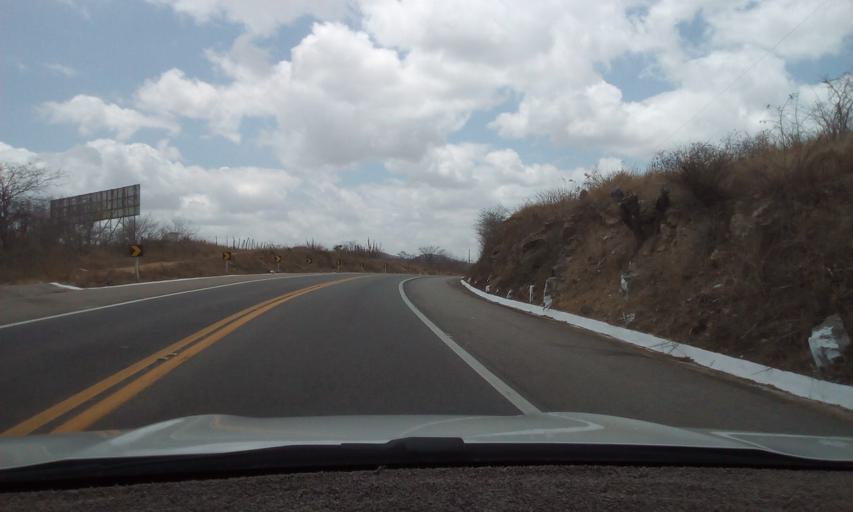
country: BR
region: Pernambuco
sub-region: Taquaritinga Do Norte
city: Taquaritinga do Norte
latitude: -7.6898
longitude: -36.0611
